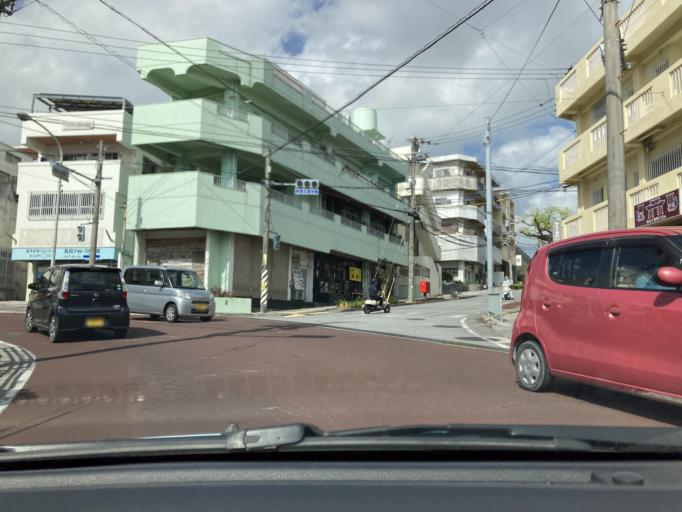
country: JP
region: Okinawa
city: Tomigusuku
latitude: 26.1981
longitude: 127.7026
